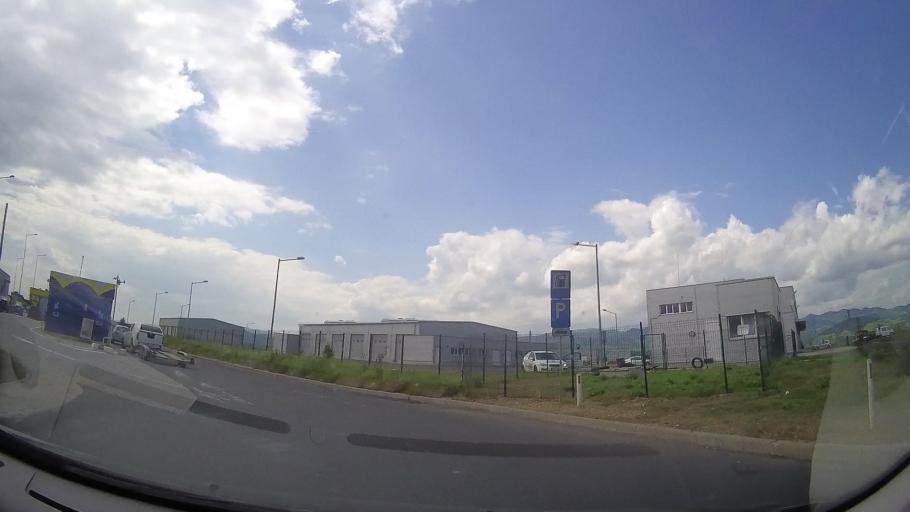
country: RO
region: Alba
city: Vurpar
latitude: 45.9656
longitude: 23.4690
